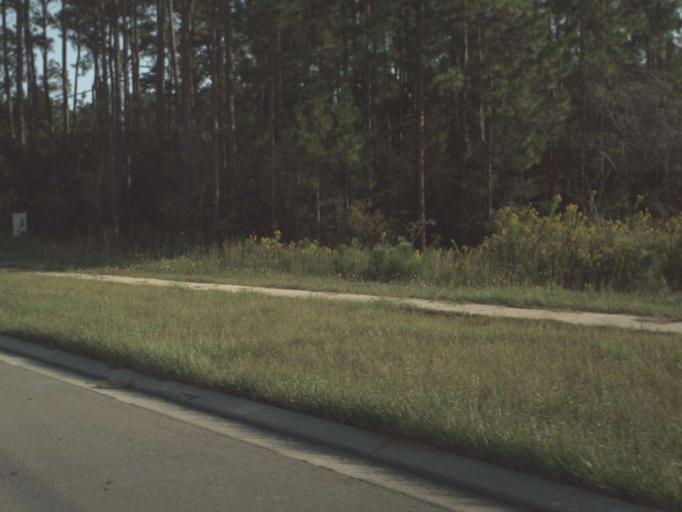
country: US
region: Florida
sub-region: Bay County
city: Laguna Beach
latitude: 30.4467
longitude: -85.8739
